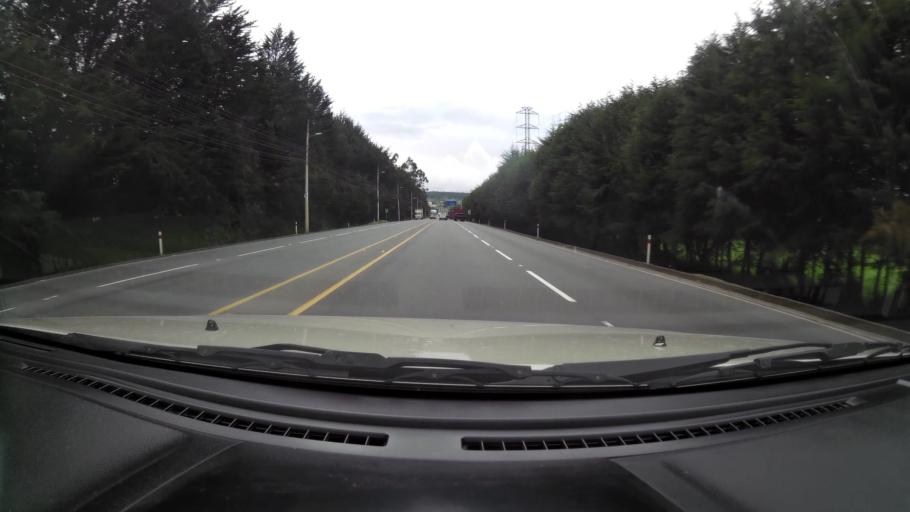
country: EC
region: Pichincha
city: Machachi
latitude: -0.4649
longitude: -78.5787
